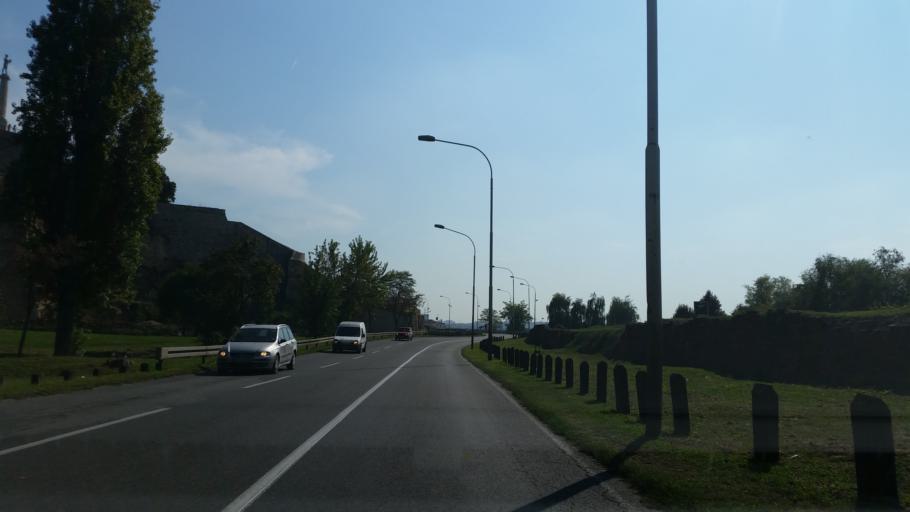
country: RS
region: Central Serbia
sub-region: Belgrade
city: Stari Grad
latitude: 44.8242
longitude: 20.4461
